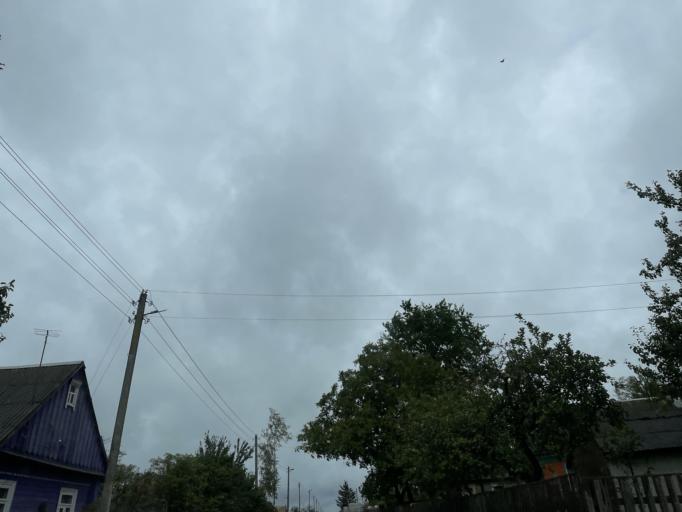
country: BY
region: Brest
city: Lyakhavichy
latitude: 53.1834
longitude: 26.2554
